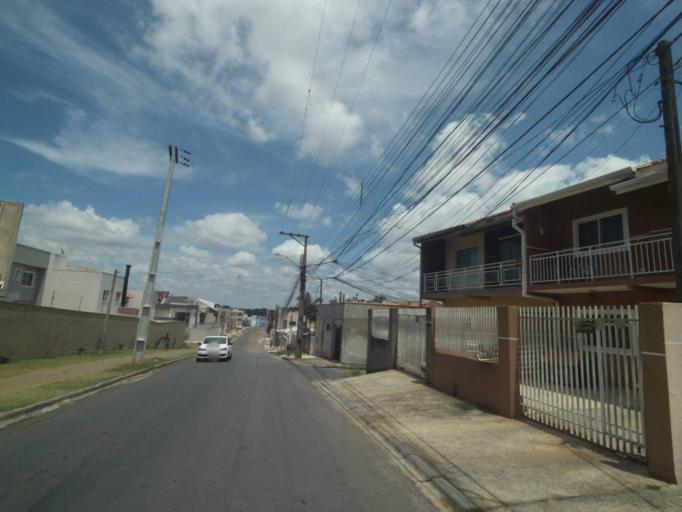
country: BR
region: Parana
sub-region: Curitiba
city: Curitiba
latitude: -25.4601
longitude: -49.3466
